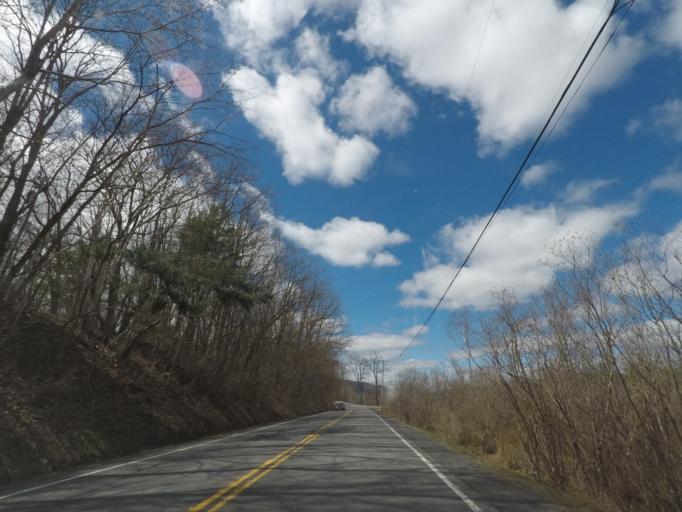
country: US
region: New York
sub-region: Albany County
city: Voorheesville
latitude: 42.6470
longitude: -73.9752
